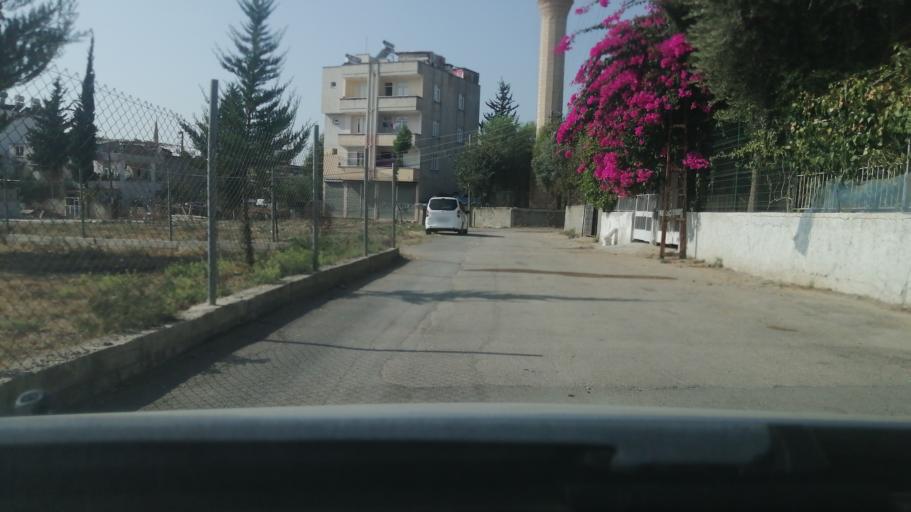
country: TR
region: Adana
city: Seyhan
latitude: 37.0183
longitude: 35.2757
